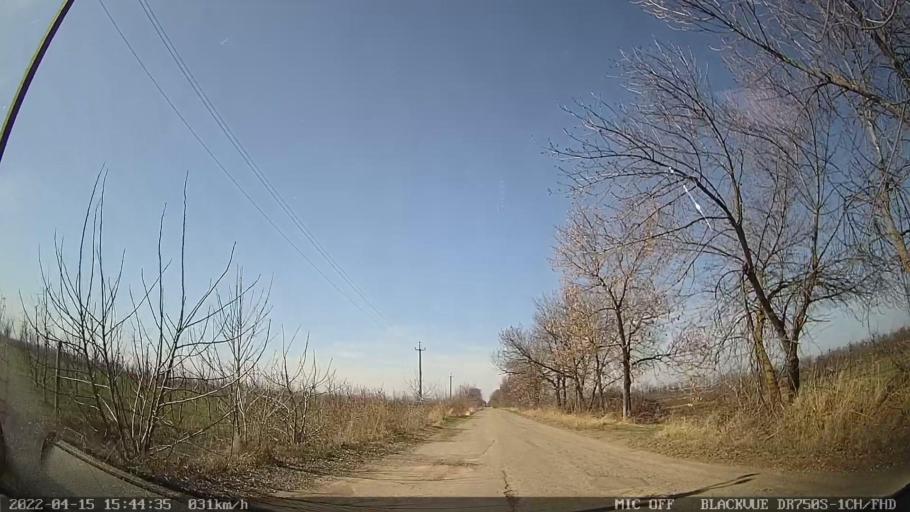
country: MD
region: Raionul Ocnita
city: Otaci
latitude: 48.3711
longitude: 27.9219
